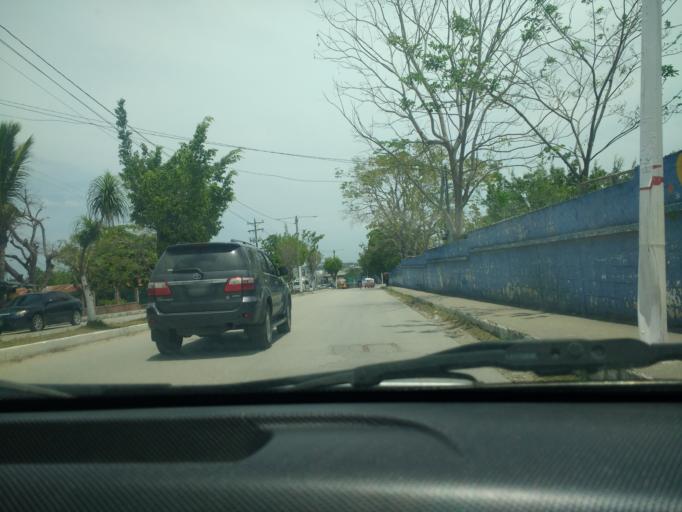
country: GT
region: Peten
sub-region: Municipio de Flores
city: Flores
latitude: 16.9197
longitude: -89.9062
